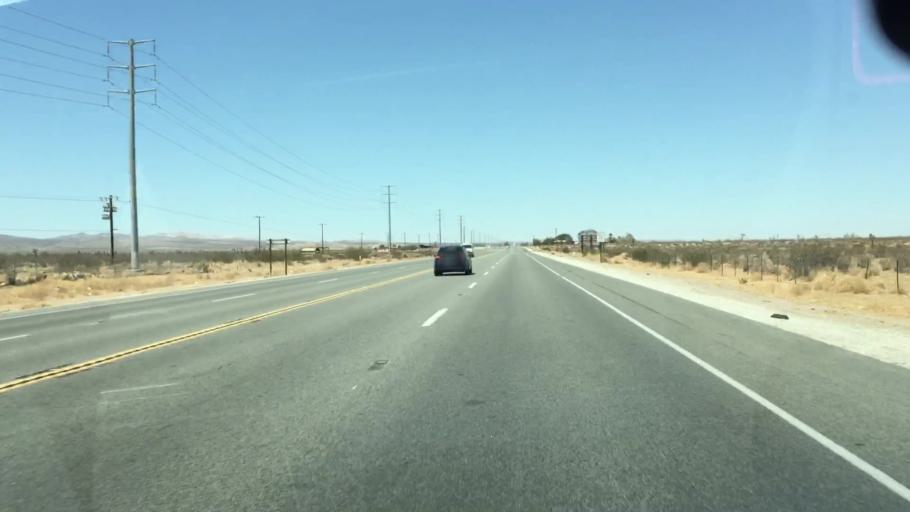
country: US
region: California
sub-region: San Bernardino County
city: Adelanto
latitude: 34.5954
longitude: -117.4175
